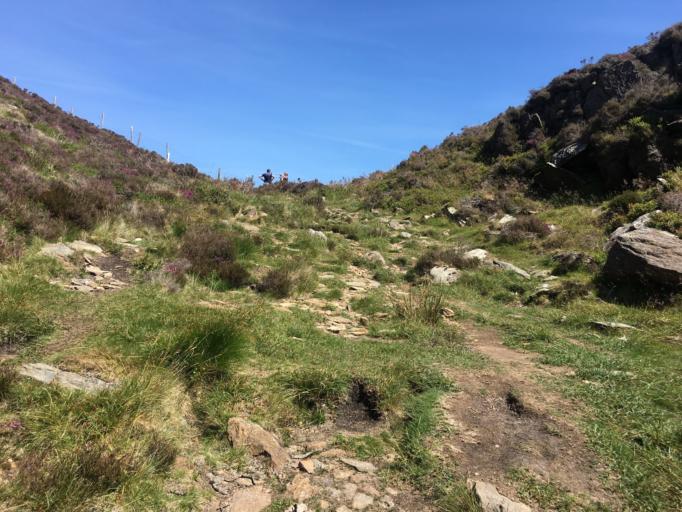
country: GB
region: Wales
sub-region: Gwynedd
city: Penrhyndeudraeth
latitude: 53.0120
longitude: -4.0784
